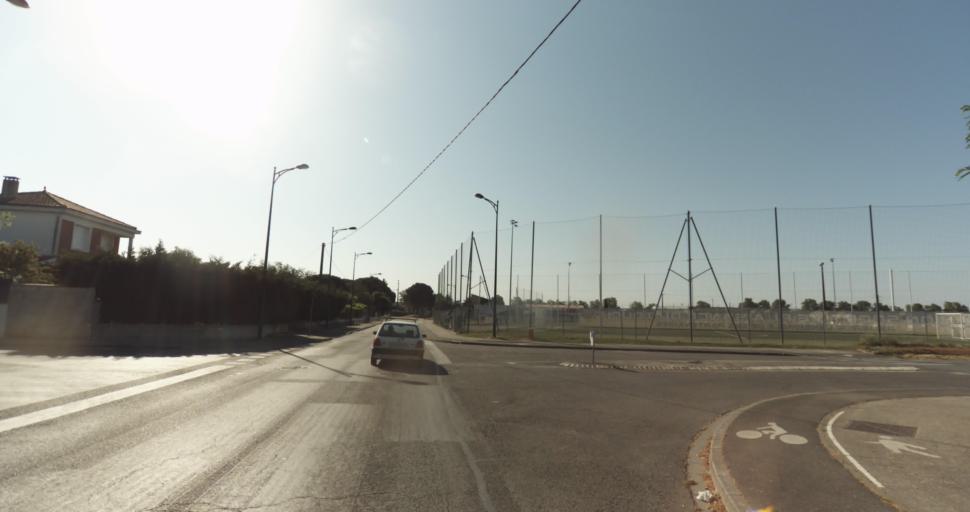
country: FR
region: Midi-Pyrenees
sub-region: Departement de la Haute-Garonne
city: Plaisance-du-Touch
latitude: 43.5657
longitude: 1.2869
